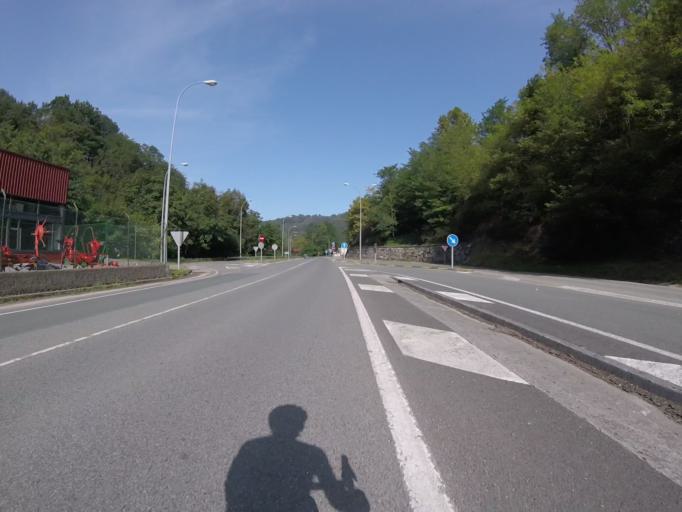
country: ES
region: Navarre
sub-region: Provincia de Navarra
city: Doneztebe
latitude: 43.1364
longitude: -1.5549
